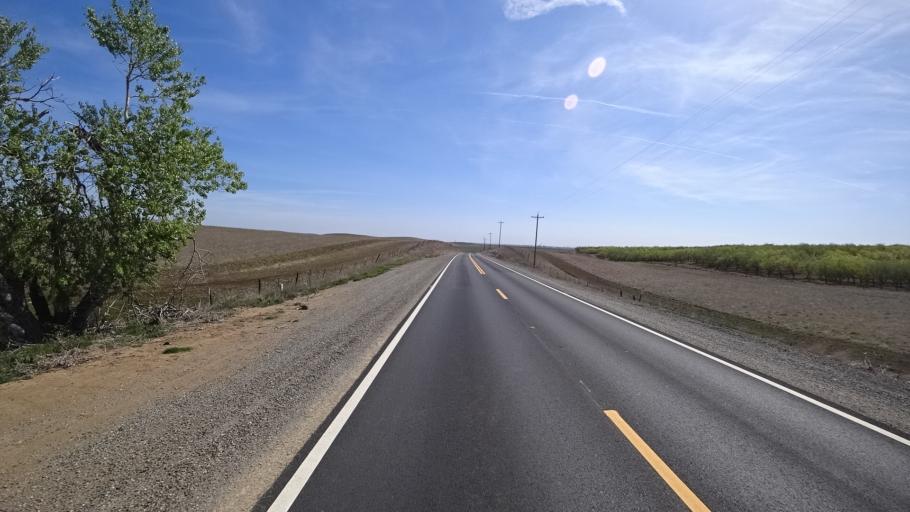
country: US
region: California
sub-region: Glenn County
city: Willows
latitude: 39.5314
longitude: -122.3210
